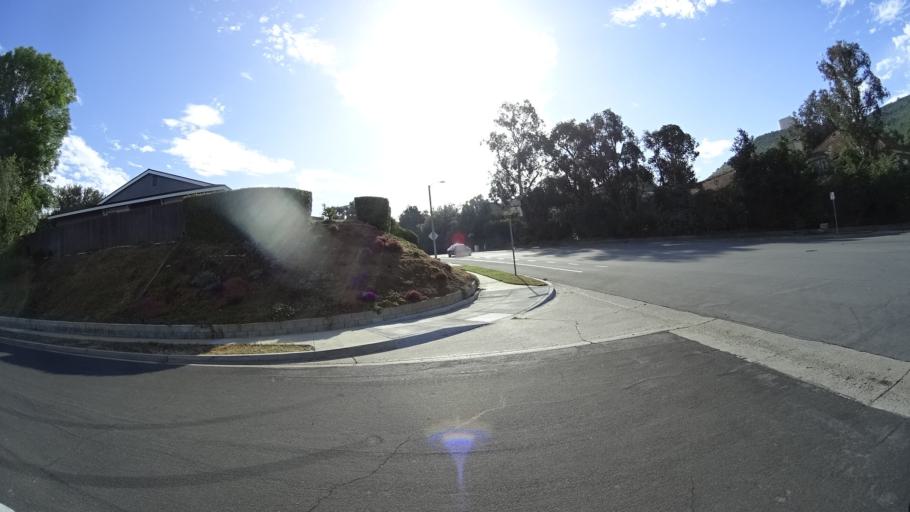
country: US
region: California
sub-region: Ventura County
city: Casa Conejo
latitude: 34.1714
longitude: -118.9538
